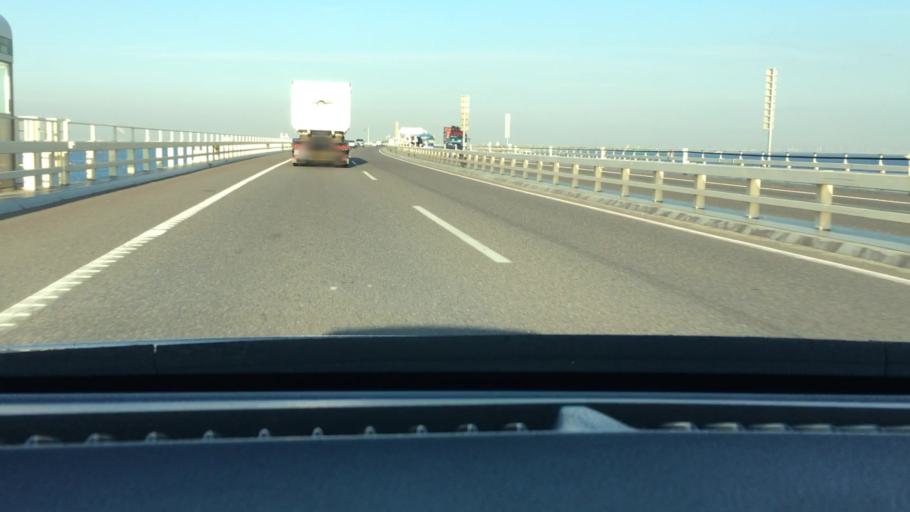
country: JP
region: Chiba
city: Kisarazu
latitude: 35.4384
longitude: 139.9124
